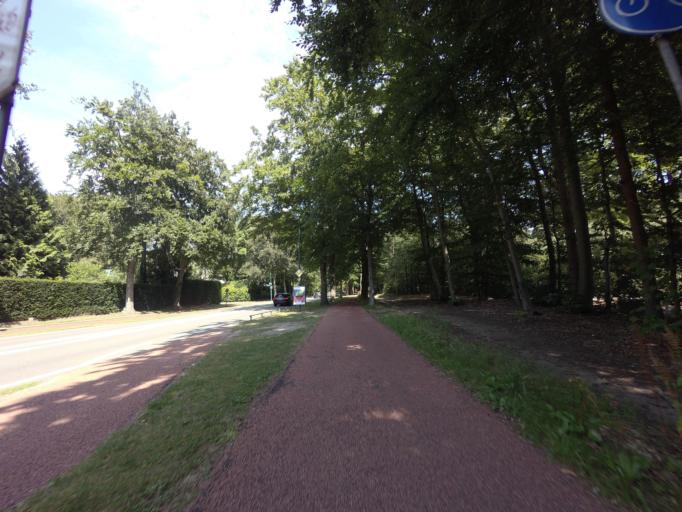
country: NL
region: Utrecht
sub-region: Gemeente Baarn
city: Baarn
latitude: 52.2036
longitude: 5.2763
